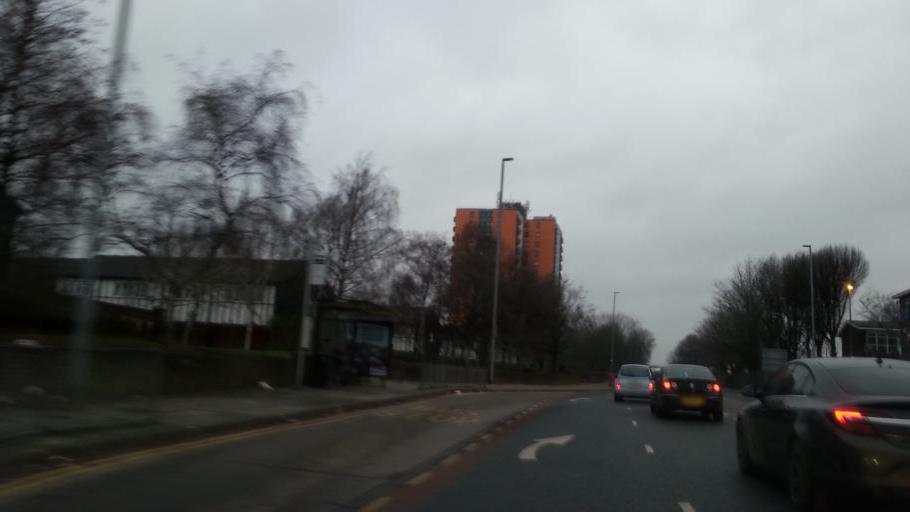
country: GB
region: England
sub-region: Manchester
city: Cheetham Hill
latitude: 53.5024
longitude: -2.2584
